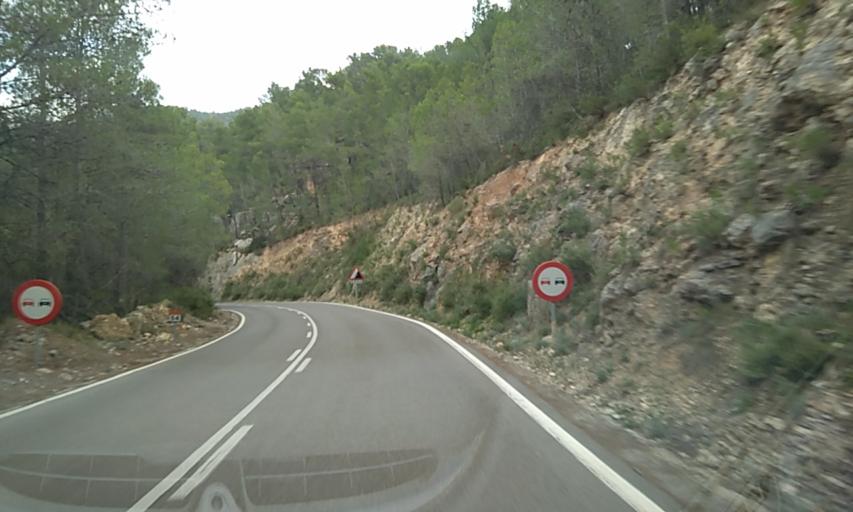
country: ES
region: Valencia
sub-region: Provincia de Castello
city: Montanejos
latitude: 40.0835
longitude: -0.5430
